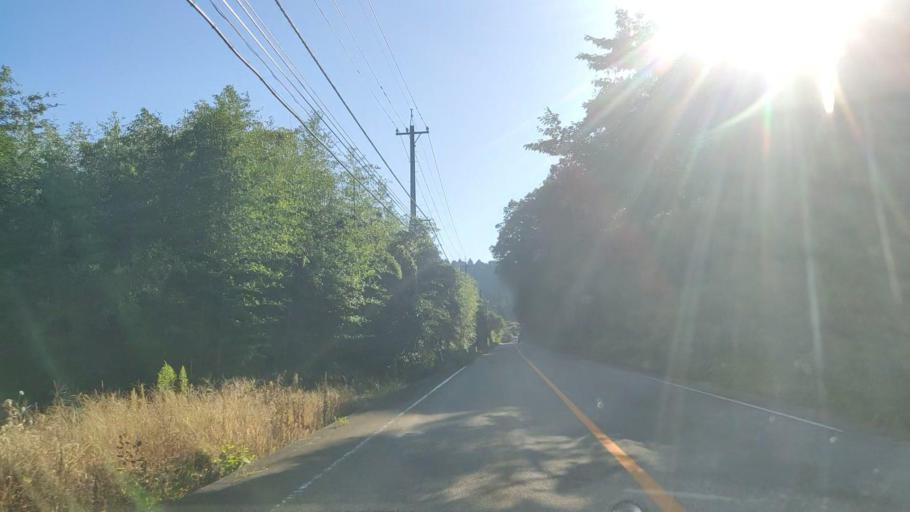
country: JP
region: Ishikawa
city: Nanao
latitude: 37.1414
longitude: 136.8694
